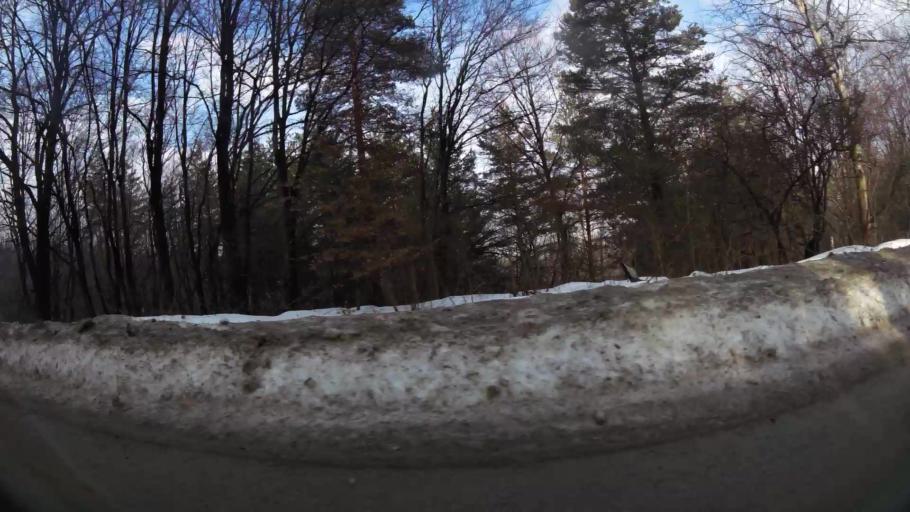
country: BG
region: Sofia-Capital
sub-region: Stolichna Obshtina
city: Sofia
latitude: 42.6456
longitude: 23.2418
